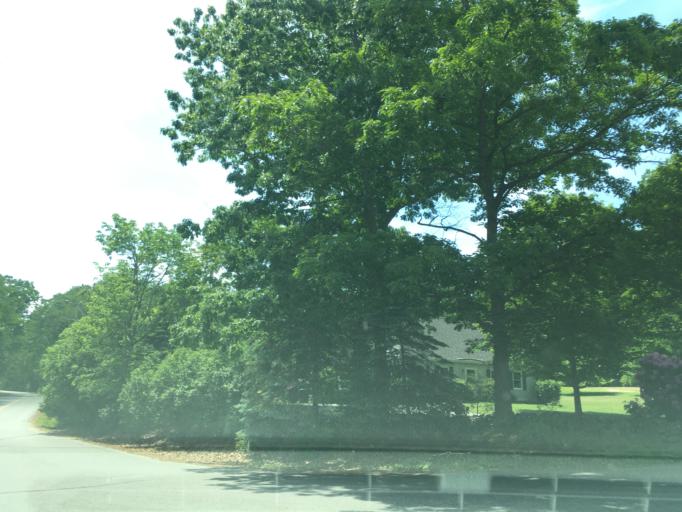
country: US
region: New Hampshire
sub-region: Rockingham County
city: Stratham Station
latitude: 43.0342
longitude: -70.8807
